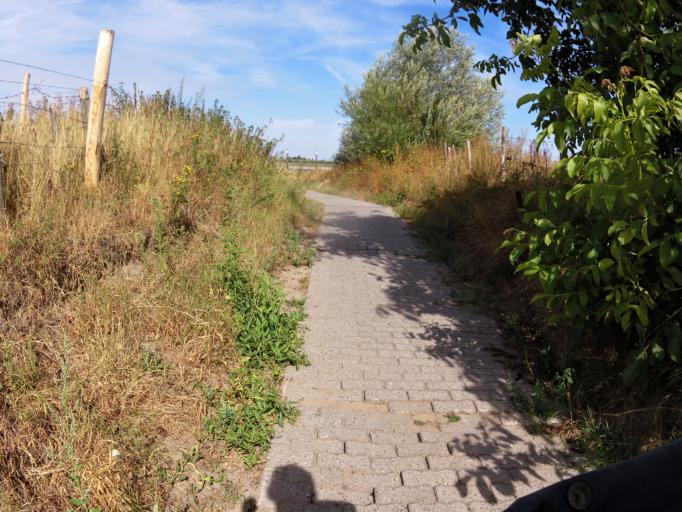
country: NL
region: Gelderland
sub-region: Gemeente Maasdriel
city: Heerewaarden
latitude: 51.8263
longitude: 5.3880
